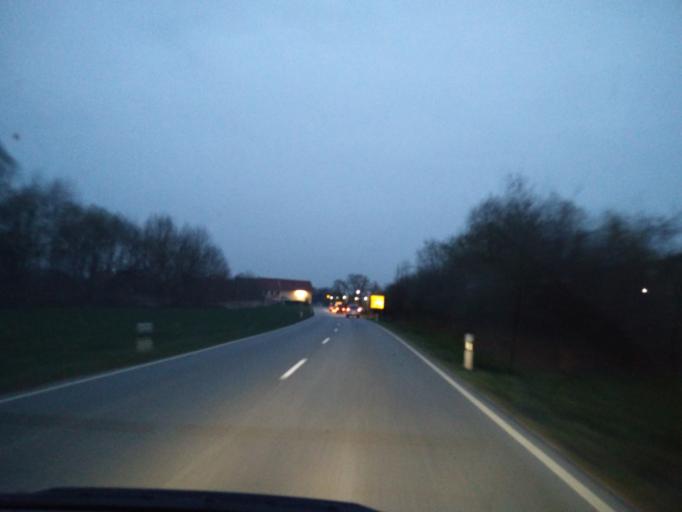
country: DE
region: Bavaria
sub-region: Upper Bavaria
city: Edling
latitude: 48.0625
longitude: 12.1702
